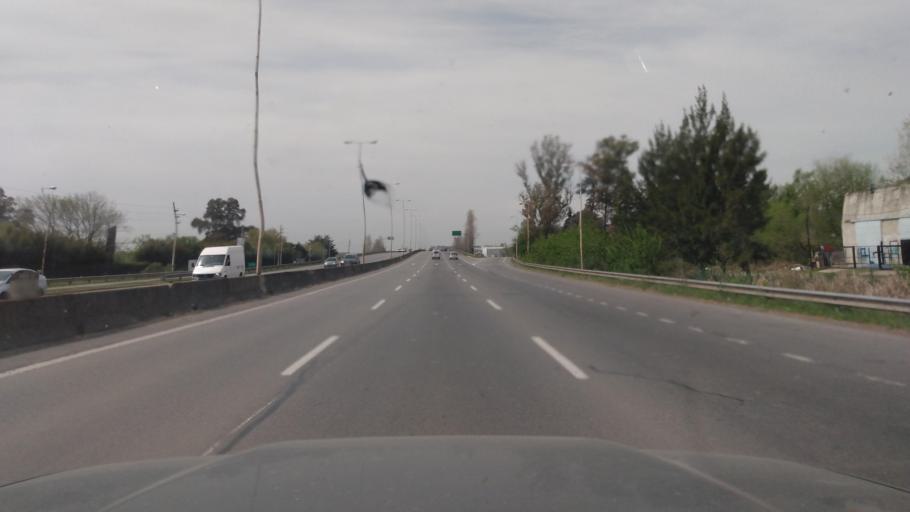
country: AR
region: Buenos Aires
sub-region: Partido de Pilar
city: Pilar
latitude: -34.4391
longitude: -58.9757
